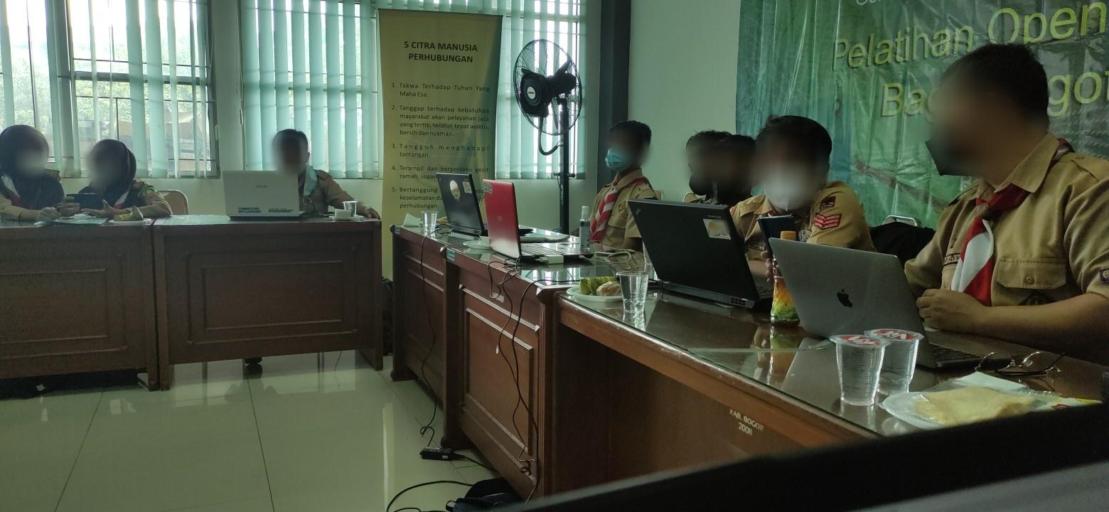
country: ID
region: West Java
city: Cibinong
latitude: -6.5295
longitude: 106.8293
